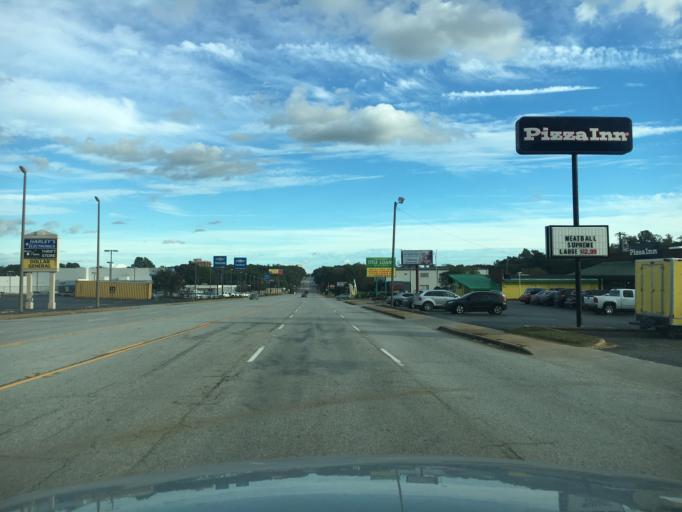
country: US
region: South Carolina
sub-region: Spartanburg County
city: Saxon
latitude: 34.9713
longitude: -81.9542
